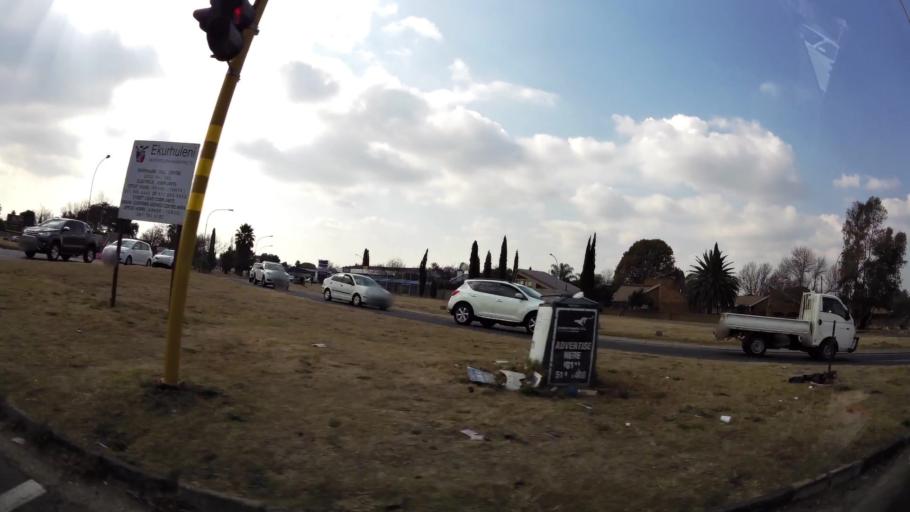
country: ZA
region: Gauteng
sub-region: Ekurhuleni Metropolitan Municipality
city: Benoni
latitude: -26.1662
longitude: 28.2790
